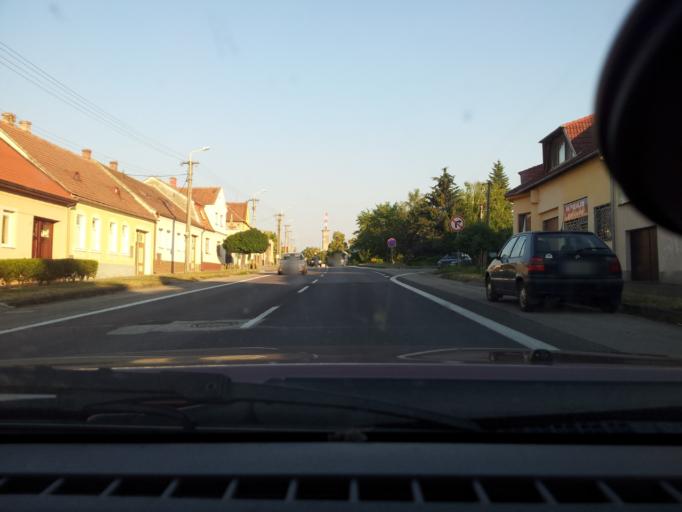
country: SK
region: Trnavsky
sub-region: Okres Skalica
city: Holic
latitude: 48.8120
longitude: 17.1632
